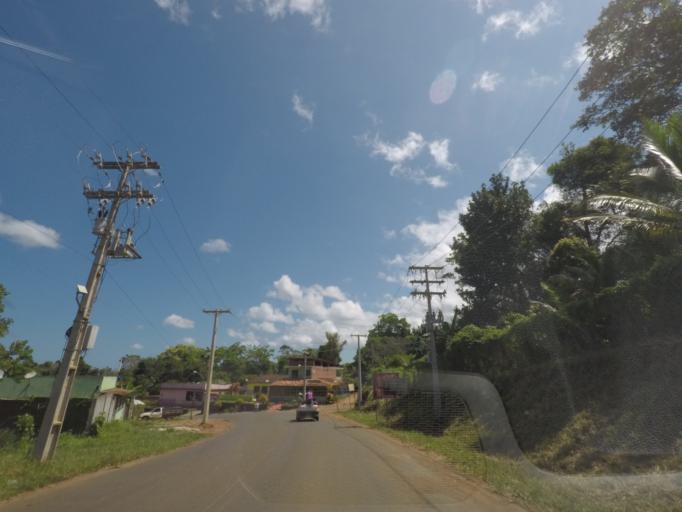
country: BR
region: Bahia
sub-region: Taperoa
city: Taperoa
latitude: -13.5304
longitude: -39.1042
